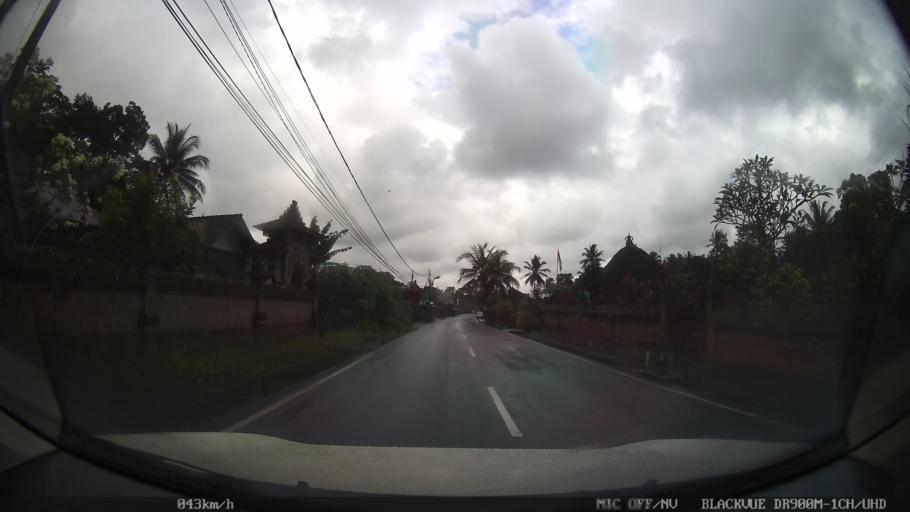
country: ID
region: Bali
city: Banjar Sayanbaleran
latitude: -8.5051
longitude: 115.1869
